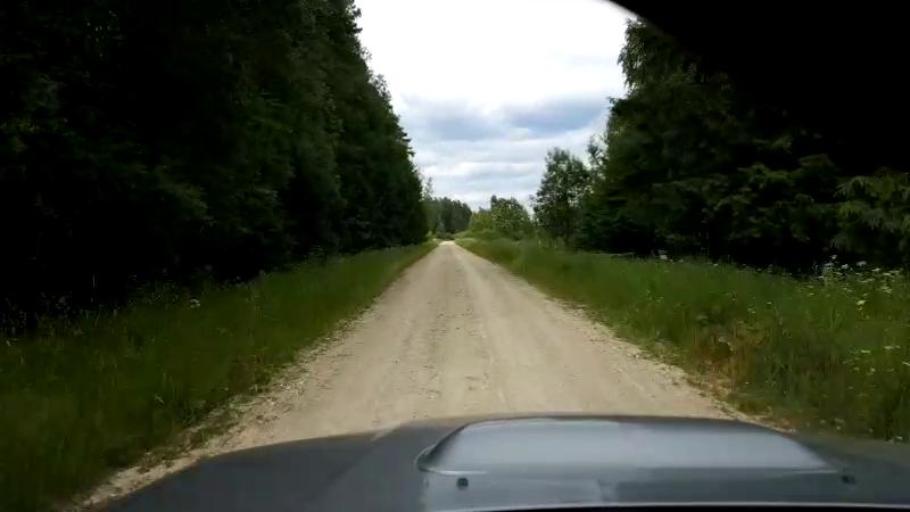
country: EE
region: Paernumaa
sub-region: Sauga vald
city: Sauga
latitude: 58.5027
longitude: 24.5804
